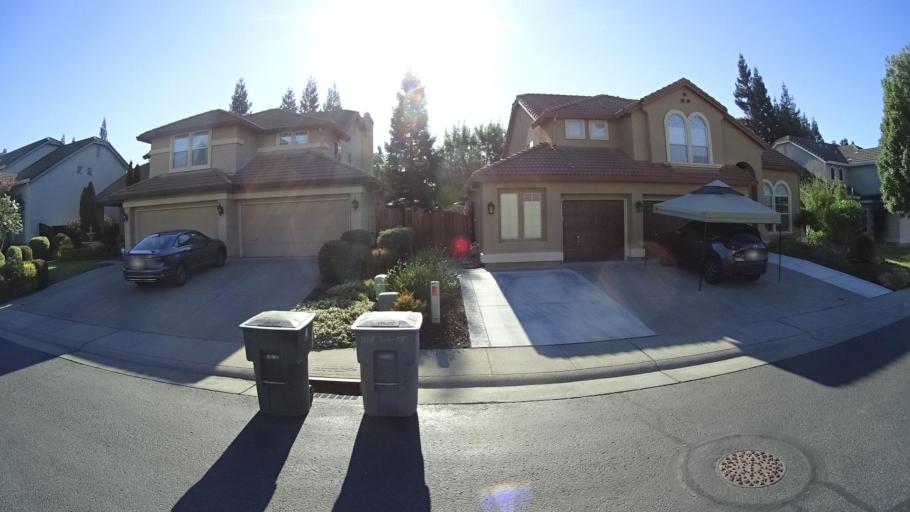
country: US
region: California
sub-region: Placer County
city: Rocklin
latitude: 38.8234
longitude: -121.2773
